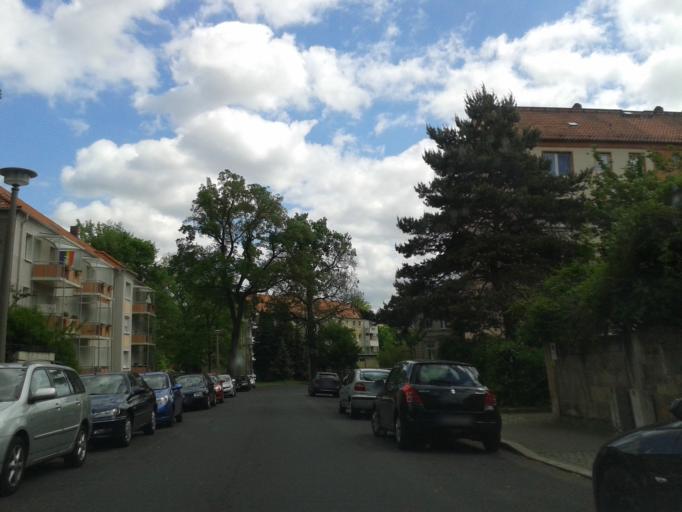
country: DE
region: Saxony
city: Dresden
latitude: 51.0367
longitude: 13.7274
